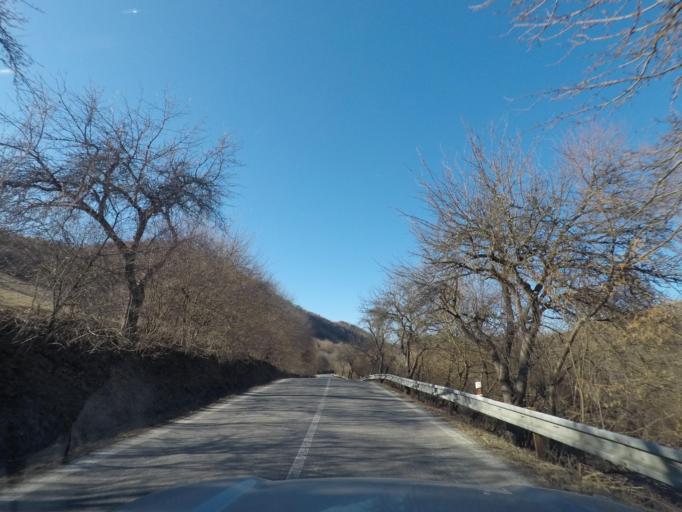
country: SK
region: Presovsky
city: Snina
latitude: 49.0787
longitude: 22.1663
